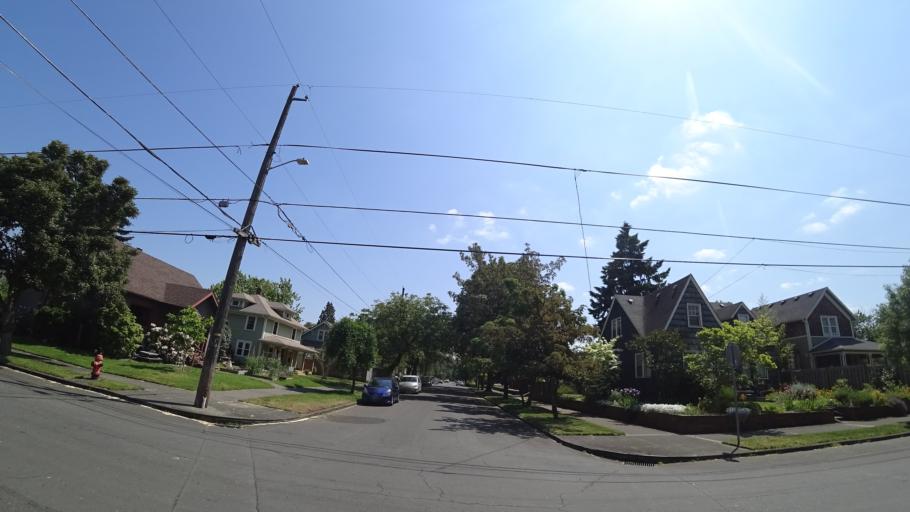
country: US
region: Oregon
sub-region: Multnomah County
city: Portland
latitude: 45.5646
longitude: -122.6533
